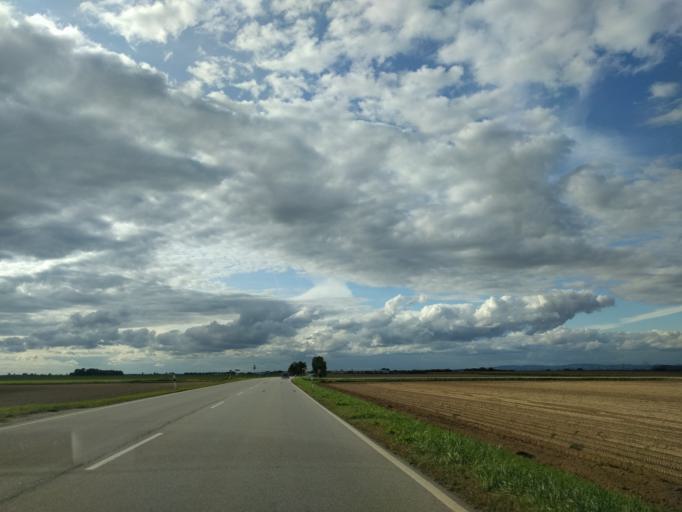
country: DE
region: Bavaria
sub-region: Lower Bavaria
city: Irlbach
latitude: 48.8162
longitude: 12.7596
